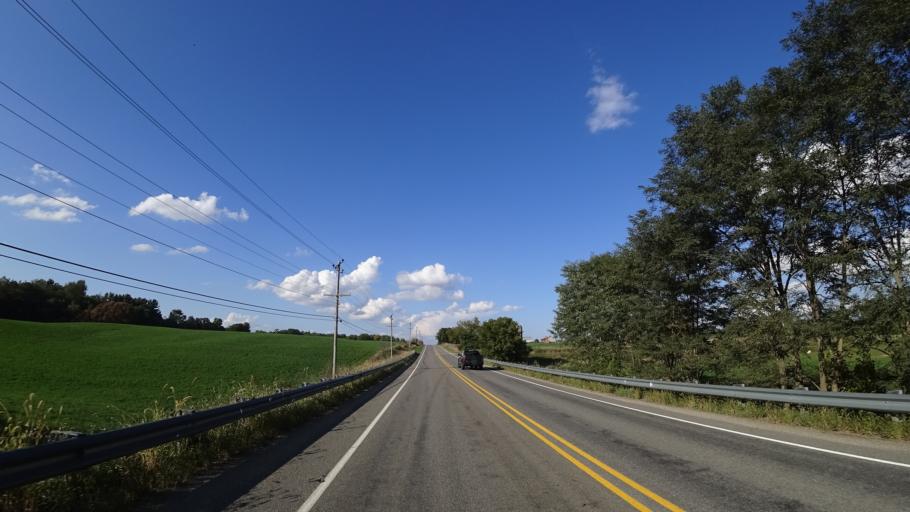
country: US
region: Michigan
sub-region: Saint Joseph County
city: Centreville
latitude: 41.8755
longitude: -85.5068
